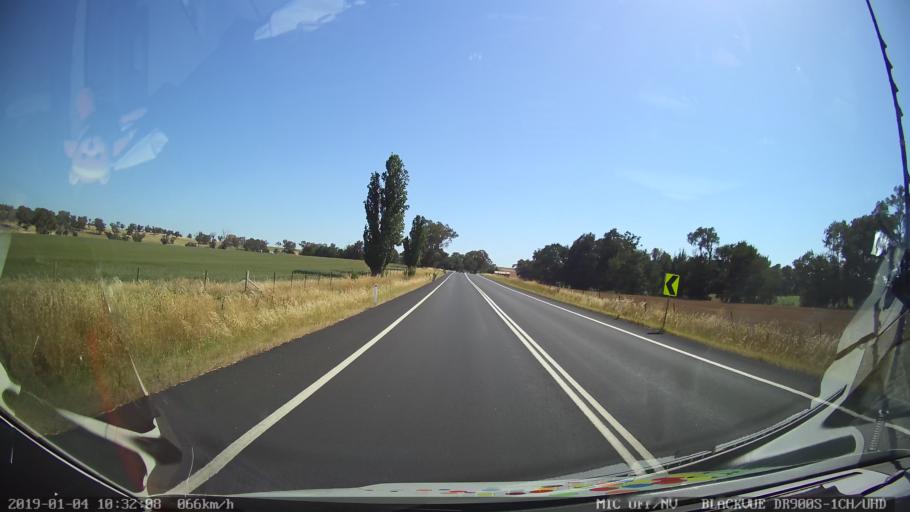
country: AU
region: New South Wales
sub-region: Cabonne
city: Canowindra
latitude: -33.3288
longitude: 148.6366
